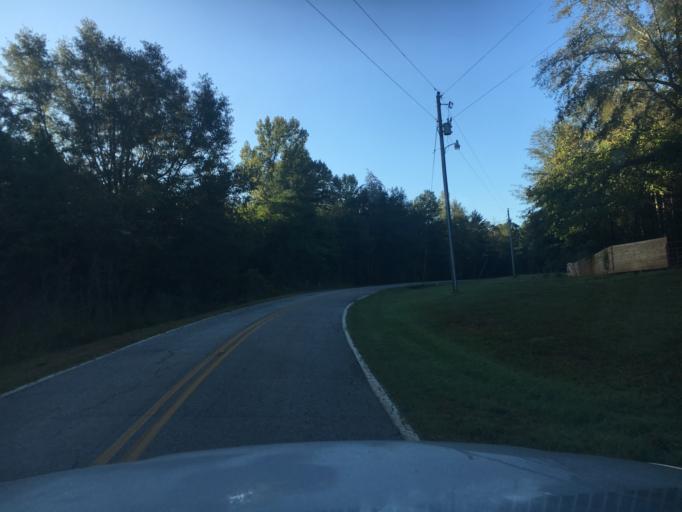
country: US
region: South Carolina
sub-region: Spartanburg County
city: Woodruff
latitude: 34.7660
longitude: -81.9615
